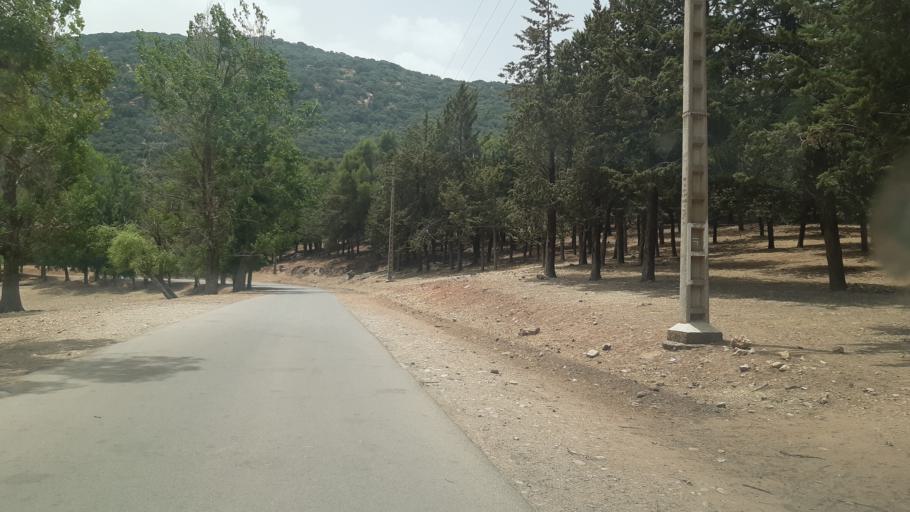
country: MA
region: Meknes-Tafilalet
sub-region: Ifrane
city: Ifrane
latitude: 33.6561
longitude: -5.0445
